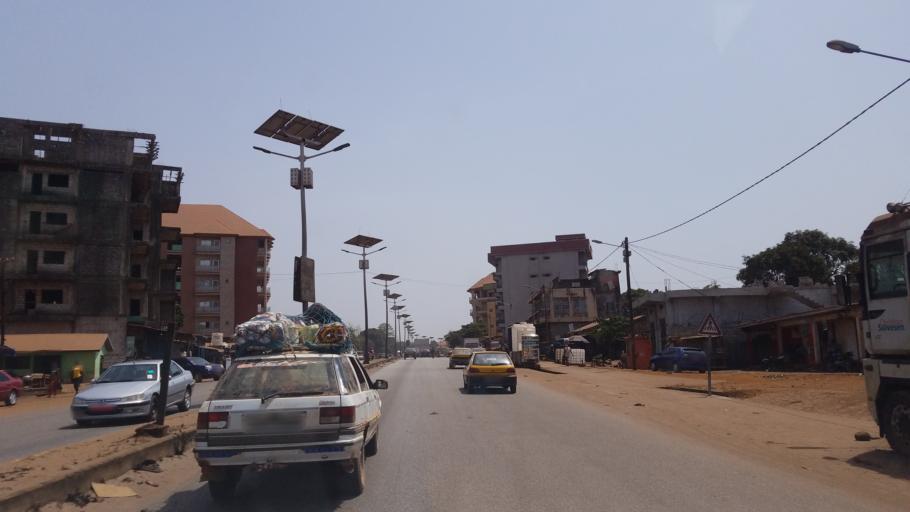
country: GN
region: Conakry
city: Conakry
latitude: 9.6478
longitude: -13.5852
